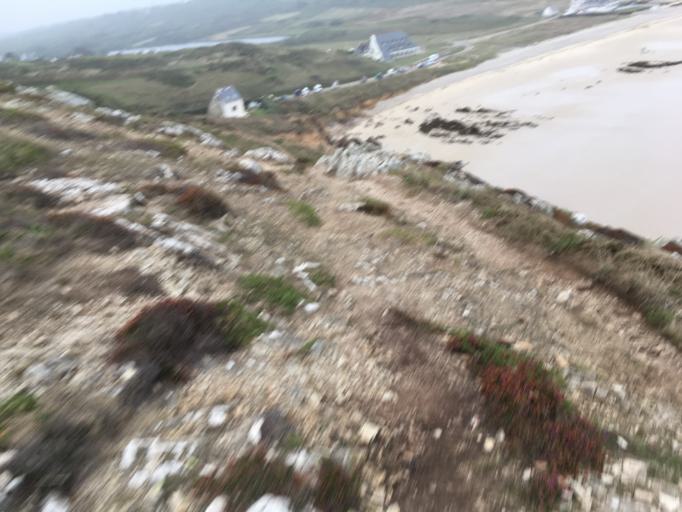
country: FR
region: Brittany
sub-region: Departement du Finistere
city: Plogoff
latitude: 48.0506
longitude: -4.7074
